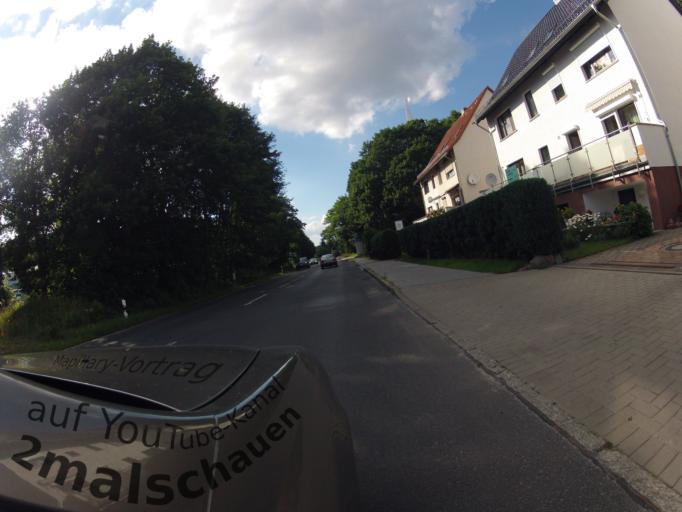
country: DE
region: Mecklenburg-Vorpommern
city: Seebad Heringsdorf
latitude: 53.9443
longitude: 14.1787
